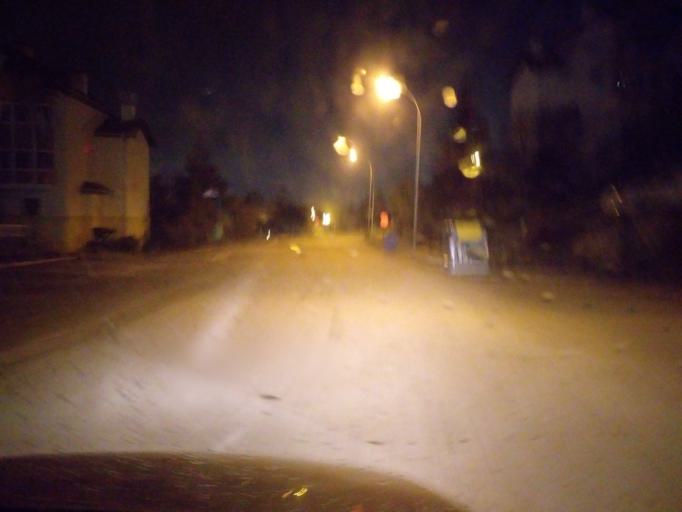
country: TR
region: Ankara
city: Batikent
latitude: 39.8764
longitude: 32.7164
